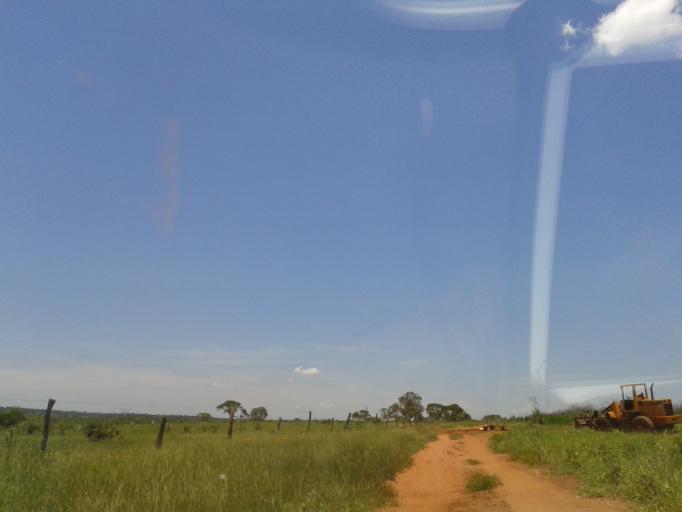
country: BR
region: Minas Gerais
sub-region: Santa Vitoria
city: Santa Vitoria
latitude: -19.2244
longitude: -50.4427
